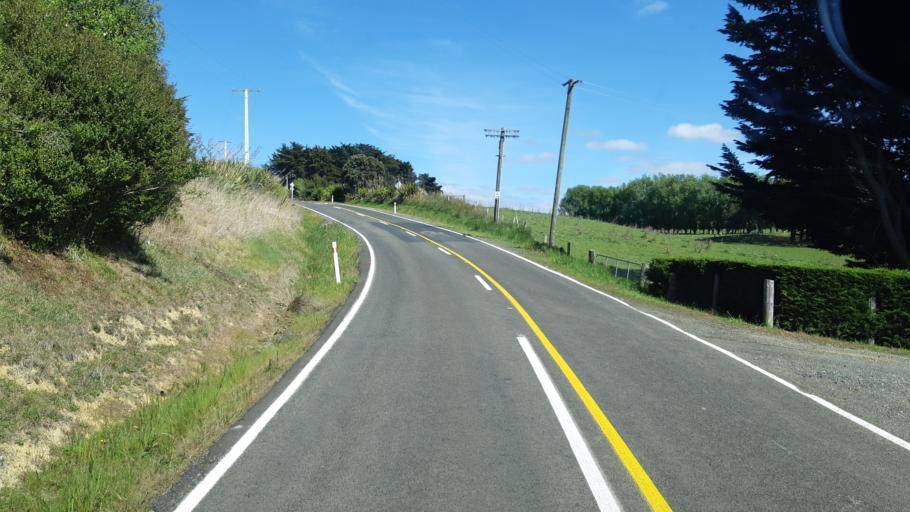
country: NZ
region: Otago
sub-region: Dunedin City
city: Portobello
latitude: -45.6550
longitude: 170.6481
